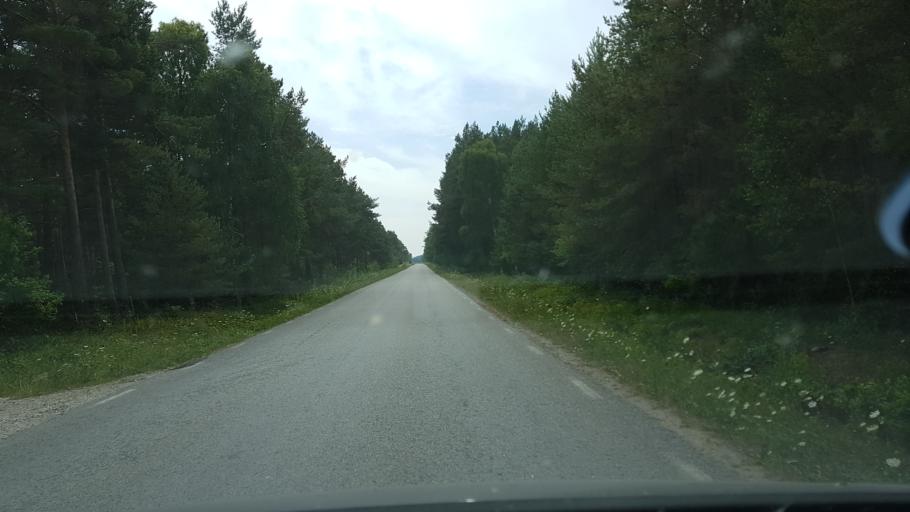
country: SE
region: Gotland
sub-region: Gotland
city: Visby
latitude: 57.7170
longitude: 18.5096
